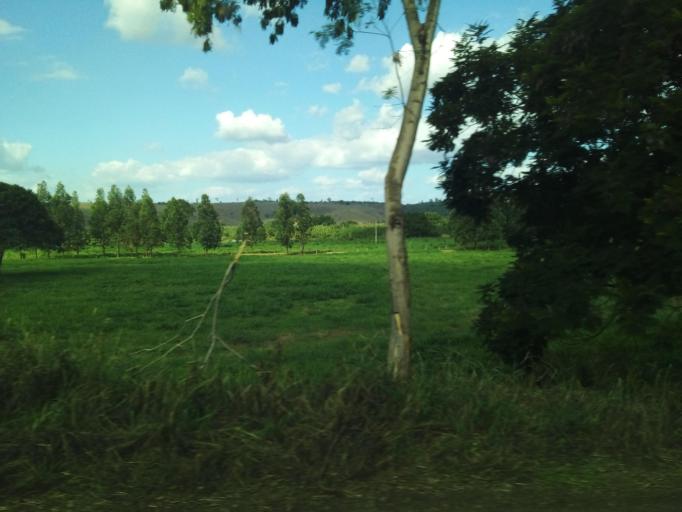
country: BR
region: Minas Gerais
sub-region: Conselheiro Pena
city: Conselheiro Pena
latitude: -18.9916
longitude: -41.5981
